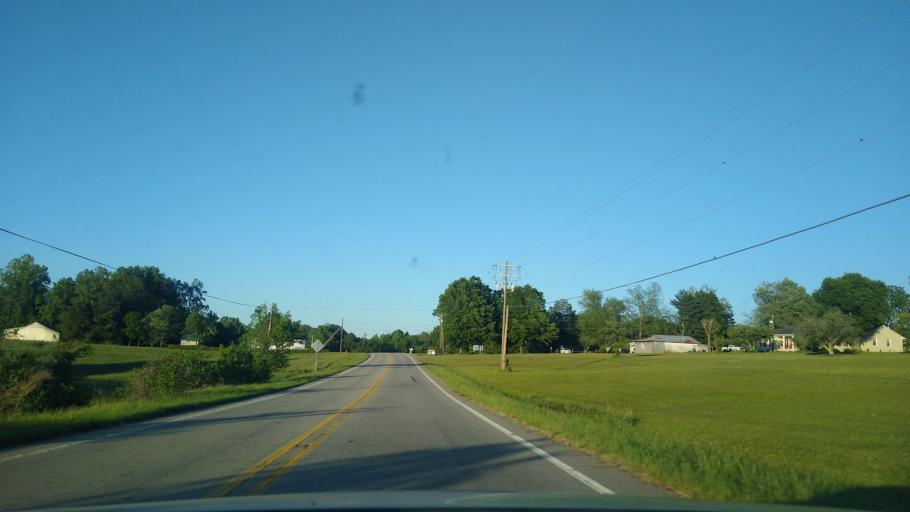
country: US
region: North Carolina
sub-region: Rockingham County
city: Reidsville
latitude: 36.3712
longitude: -79.6004
